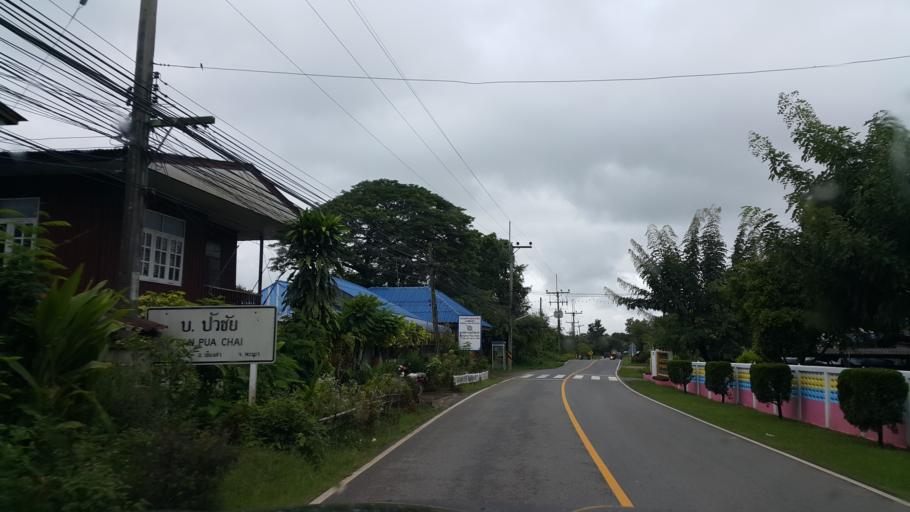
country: TH
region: Phayao
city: Chiang Kham
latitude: 19.5253
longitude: 100.3297
